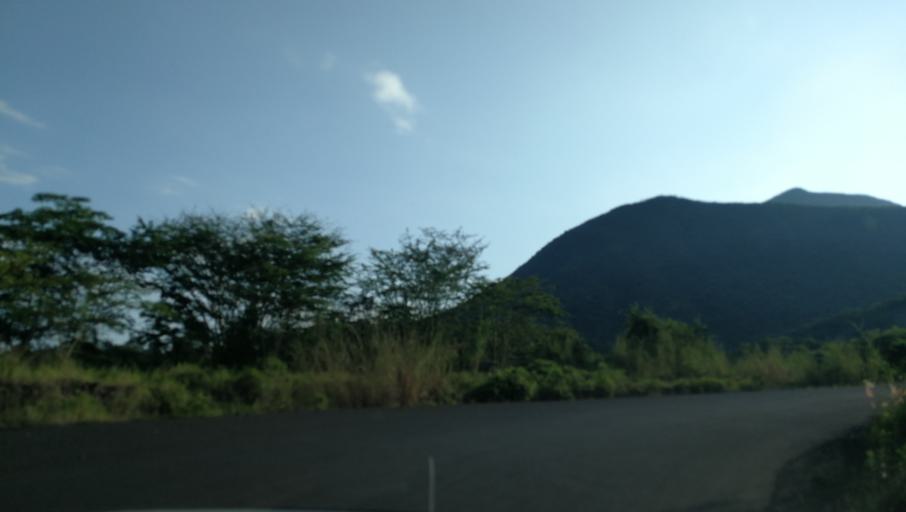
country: ET
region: Southern Nations, Nationalities, and People's Region
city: Areka
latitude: 6.8362
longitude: 37.2814
